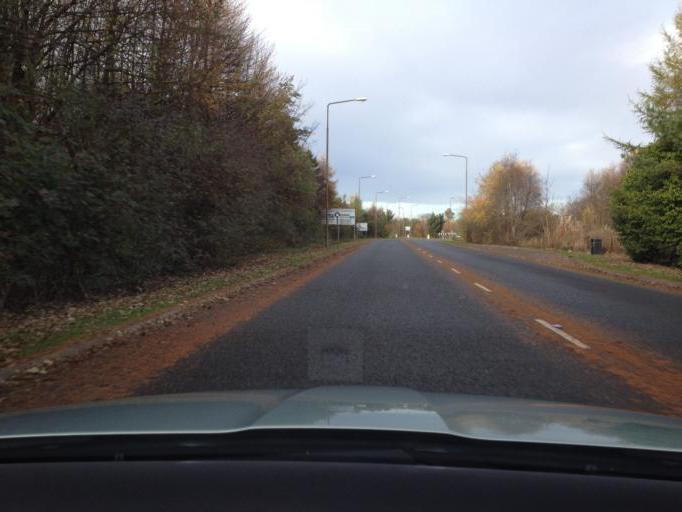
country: GB
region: Scotland
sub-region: West Lothian
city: Livingston
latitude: 55.8937
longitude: -3.5599
